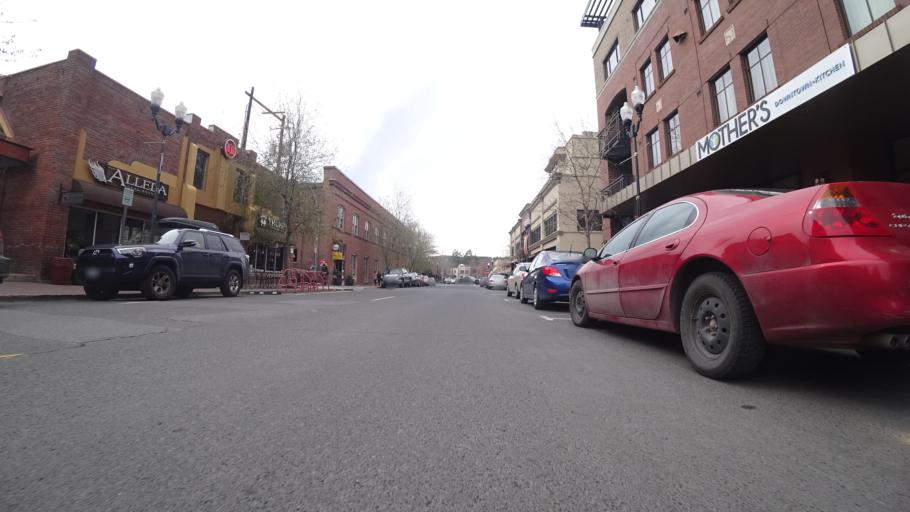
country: US
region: Oregon
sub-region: Deschutes County
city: Bend
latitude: 44.0577
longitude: -121.3123
